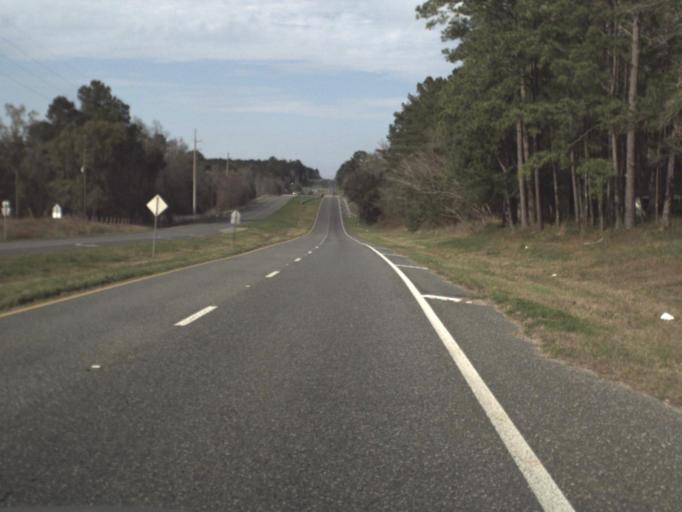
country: US
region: Florida
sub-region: Jefferson County
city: Monticello
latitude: 30.4917
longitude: -83.8815
